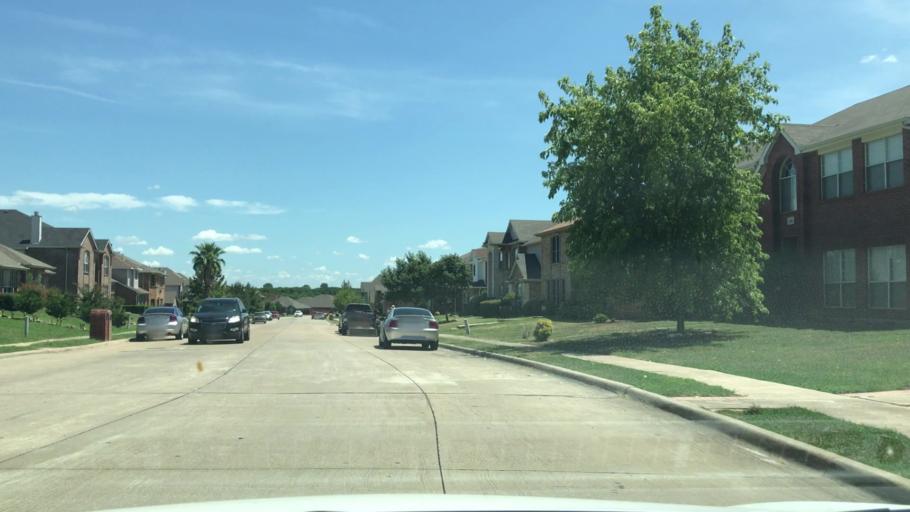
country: US
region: Texas
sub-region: Rockwall County
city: Rockwall
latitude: 32.8946
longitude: -96.4580
